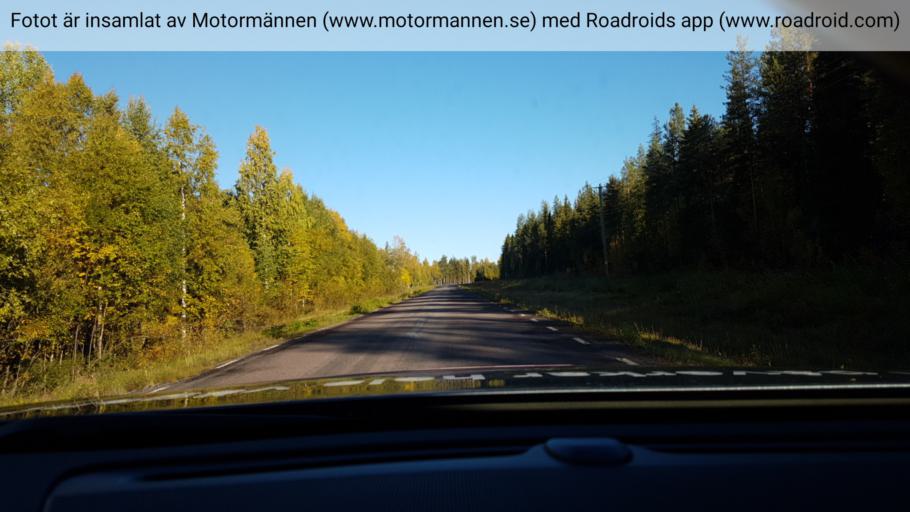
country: SE
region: Norrbotten
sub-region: Bodens Kommun
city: Boden
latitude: 66.0795
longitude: 21.3874
